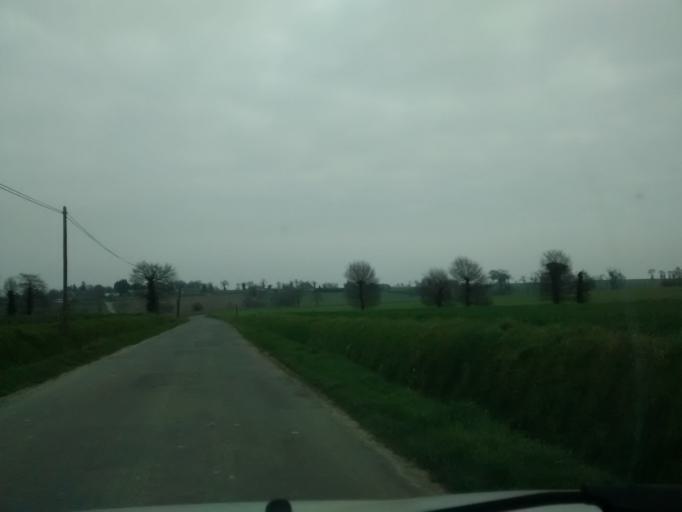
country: FR
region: Brittany
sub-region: Departement d'Ille-et-Vilaine
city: Bazouges-la-Perouse
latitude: 48.4035
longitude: -1.5663
